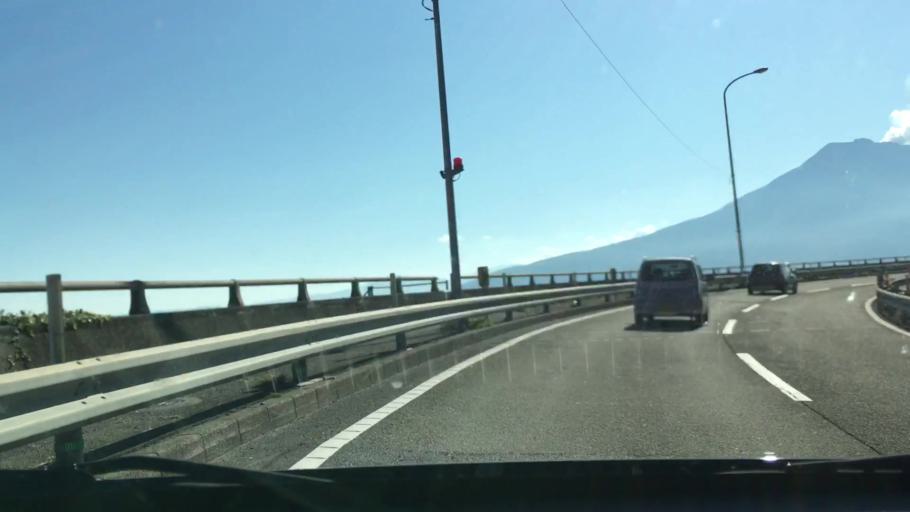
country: JP
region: Kagoshima
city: Kajiki
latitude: 31.6589
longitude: 130.6192
